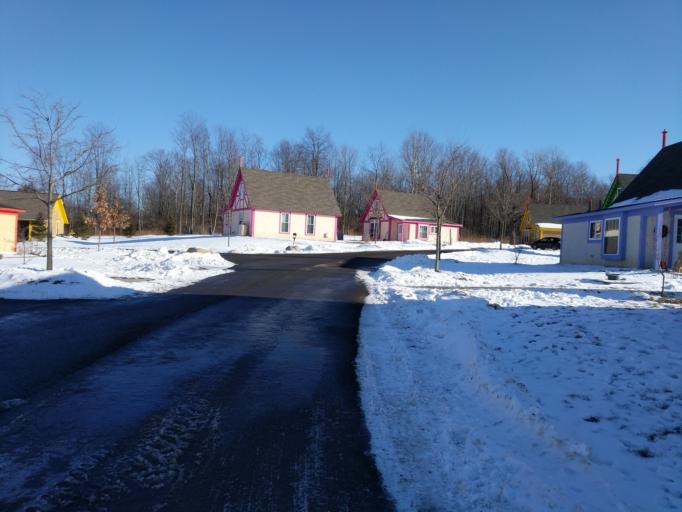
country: US
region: New York
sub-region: Tompkins County
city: Dryden
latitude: 42.3874
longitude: -76.3593
